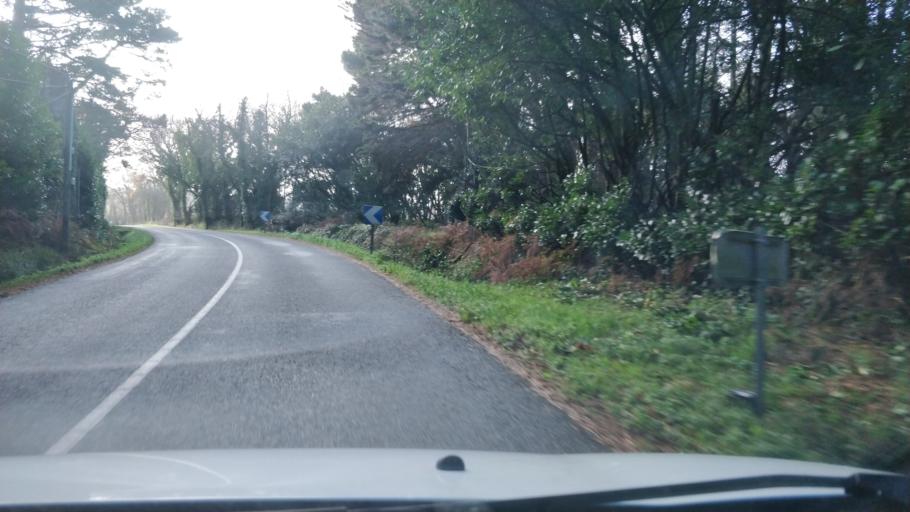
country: FR
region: Pays de la Loire
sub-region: Departement de la Loire-Atlantique
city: Saint-Molf
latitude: 47.3714
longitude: -2.4335
